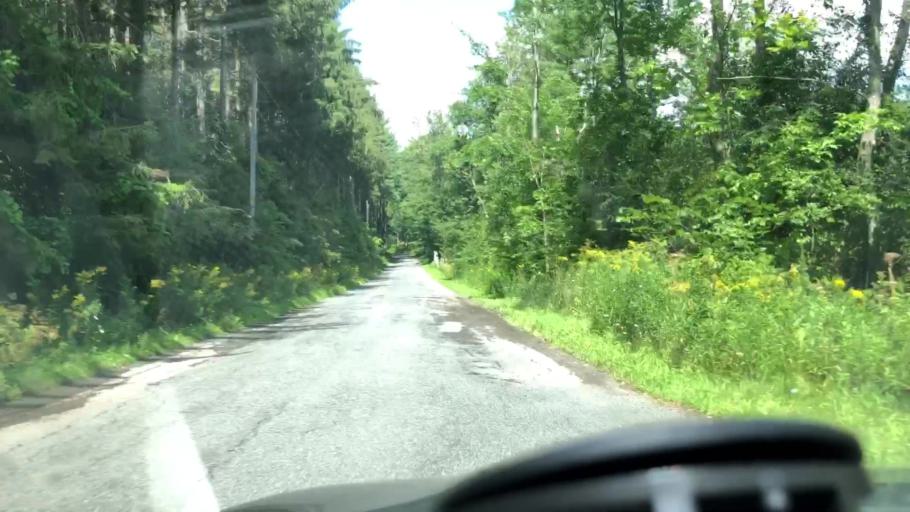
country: US
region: Massachusetts
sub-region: Berkshire County
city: North Adams
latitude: 42.6773
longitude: -73.1389
